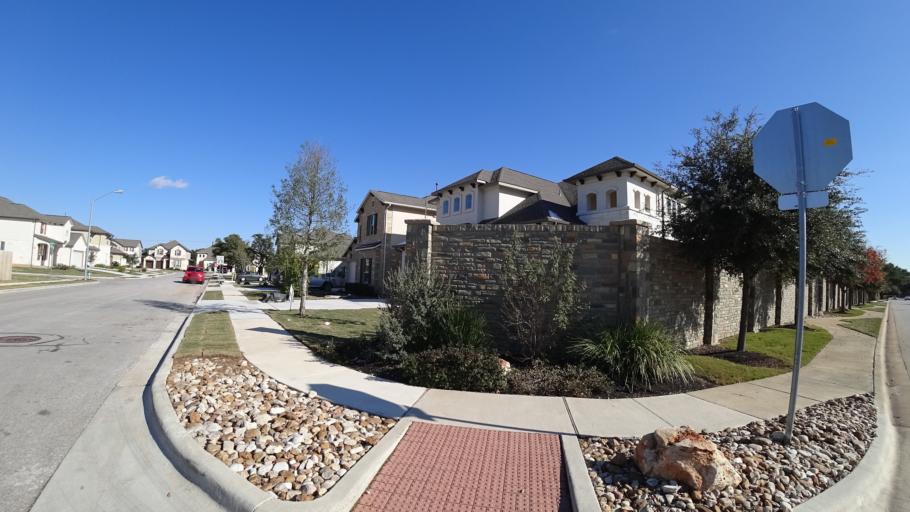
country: US
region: Texas
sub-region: Williamson County
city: Brushy Creek
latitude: 30.4911
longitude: -97.7223
